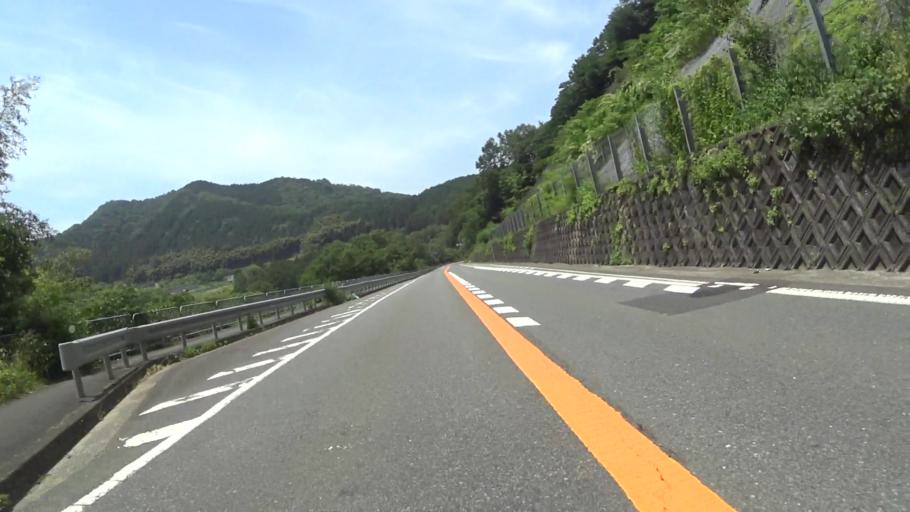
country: JP
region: Kyoto
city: Ayabe
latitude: 35.2016
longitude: 135.2483
